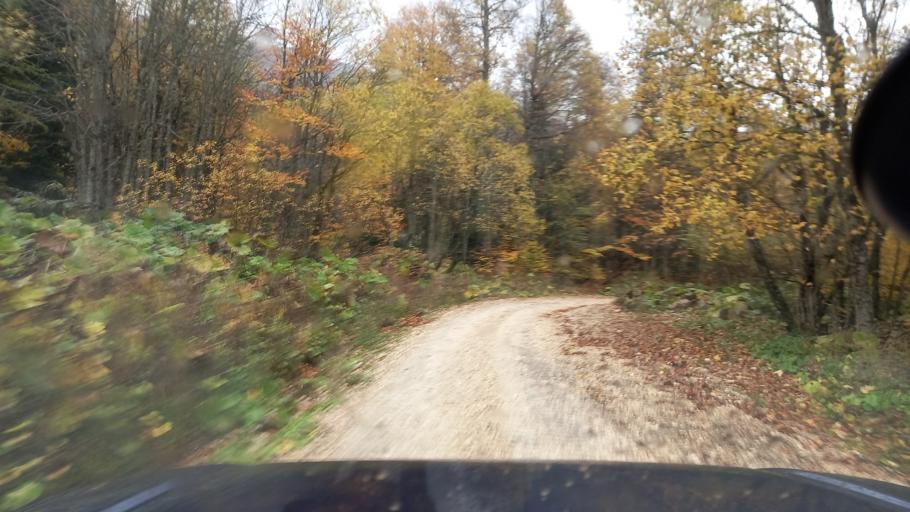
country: RU
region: Krasnodarskiy
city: Neftegorsk
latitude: 44.0281
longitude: 39.8409
